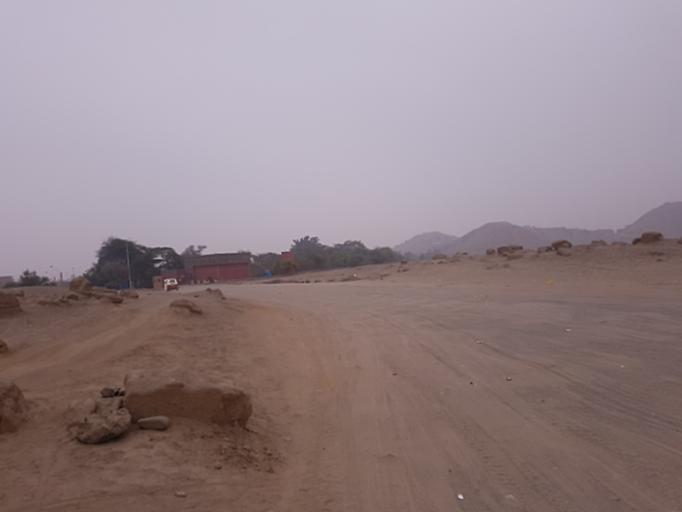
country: PE
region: Lima
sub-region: Lima
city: Santa Maria
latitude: -11.9864
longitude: -76.9128
